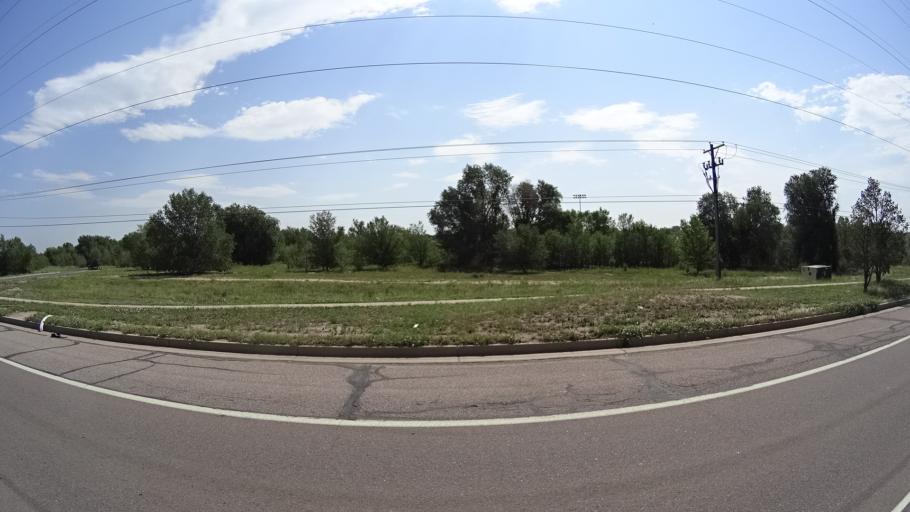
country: US
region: Colorado
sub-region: El Paso County
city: Stratmoor
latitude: 38.8018
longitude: -104.7575
